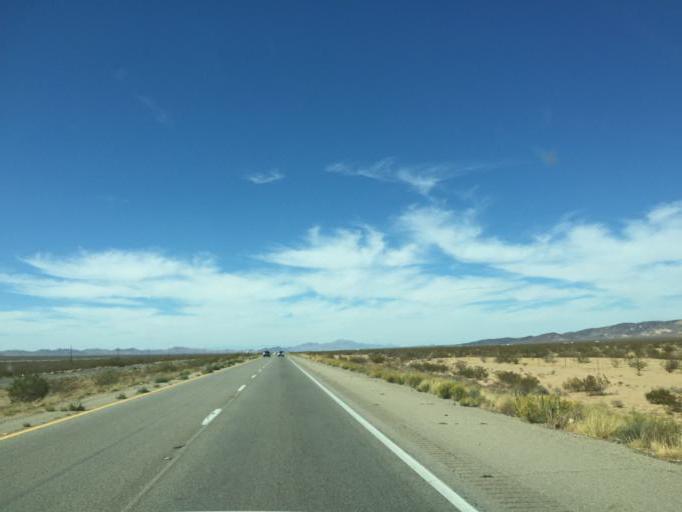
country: US
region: Arizona
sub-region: Mohave County
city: Dolan Springs
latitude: 35.5730
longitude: -114.3822
